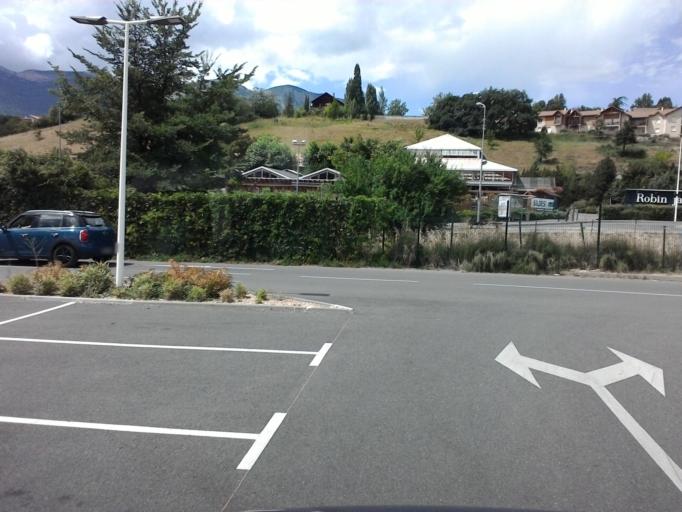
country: FR
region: Provence-Alpes-Cote d'Azur
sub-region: Departement des Hautes-Alpes
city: Gap
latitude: 44.5681
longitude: 6.0967
